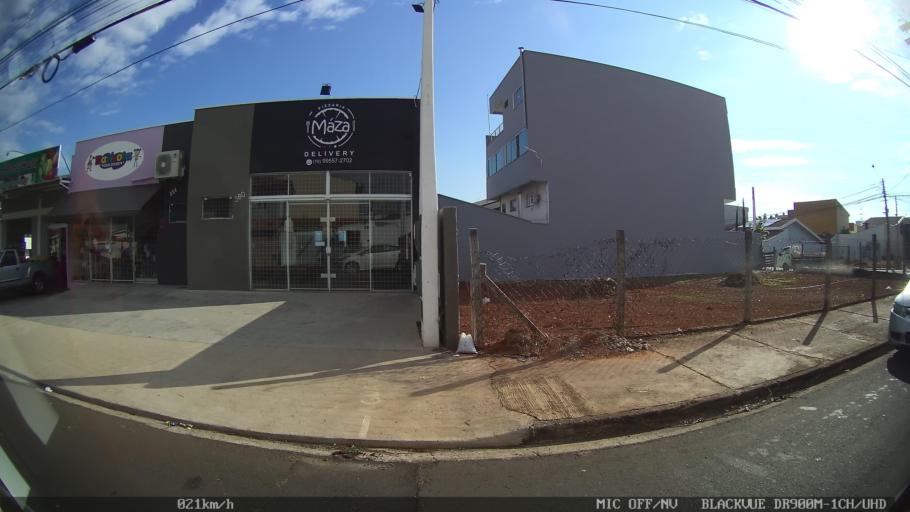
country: BR
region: Sao Paulo
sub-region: Americana
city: Americana
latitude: -22.7336
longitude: -47.3622
